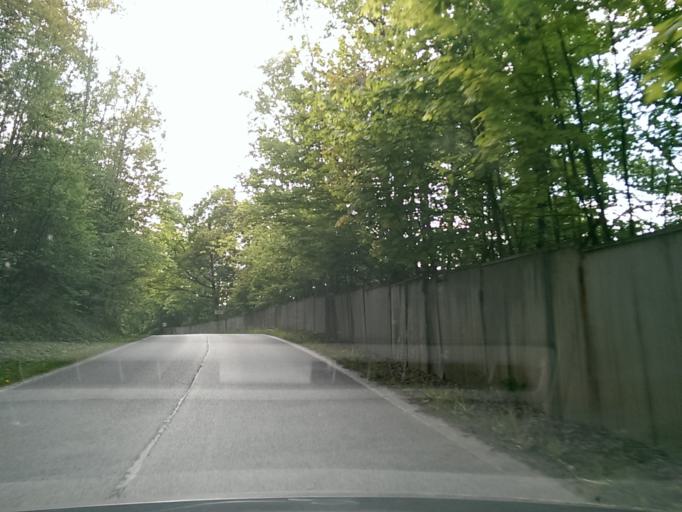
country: CZ
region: Central Bohemia
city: Bela pod Bezdezem
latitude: 50.4991
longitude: 14.8737
